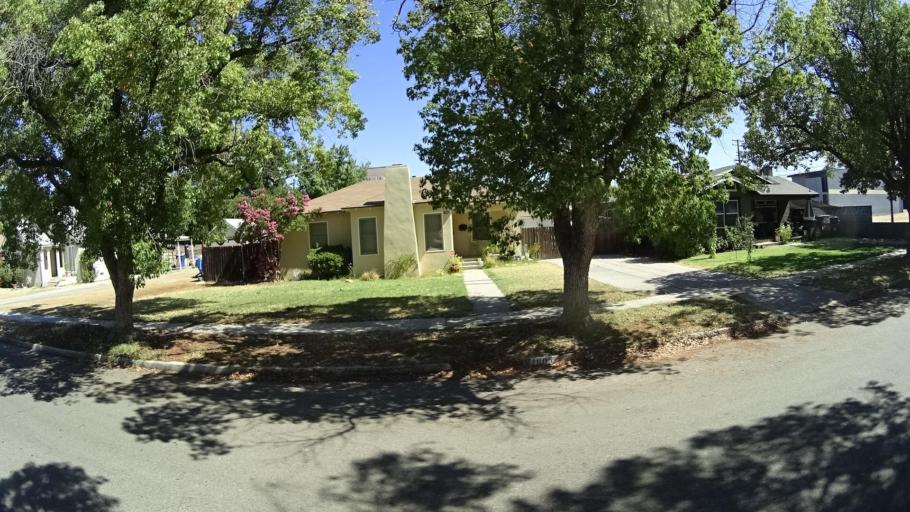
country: US
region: California
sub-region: Fresno County
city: Fresno
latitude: 36.7768
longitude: -119.7918
